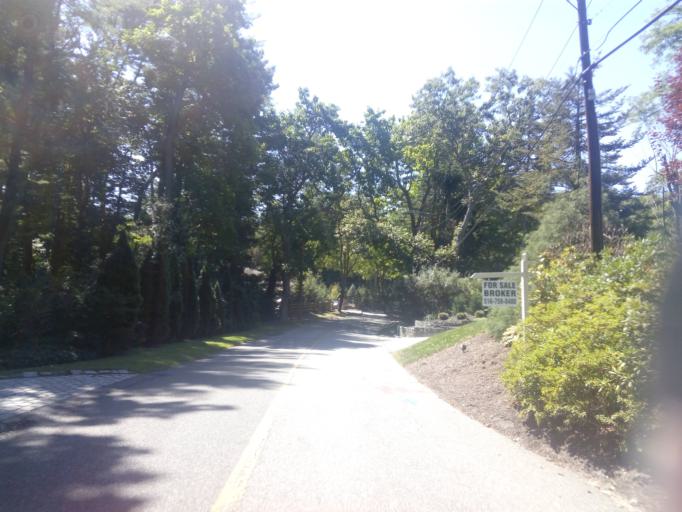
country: US
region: New York
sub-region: Nassau County
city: Upper Brookville
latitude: 40.8448
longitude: -73.5717
